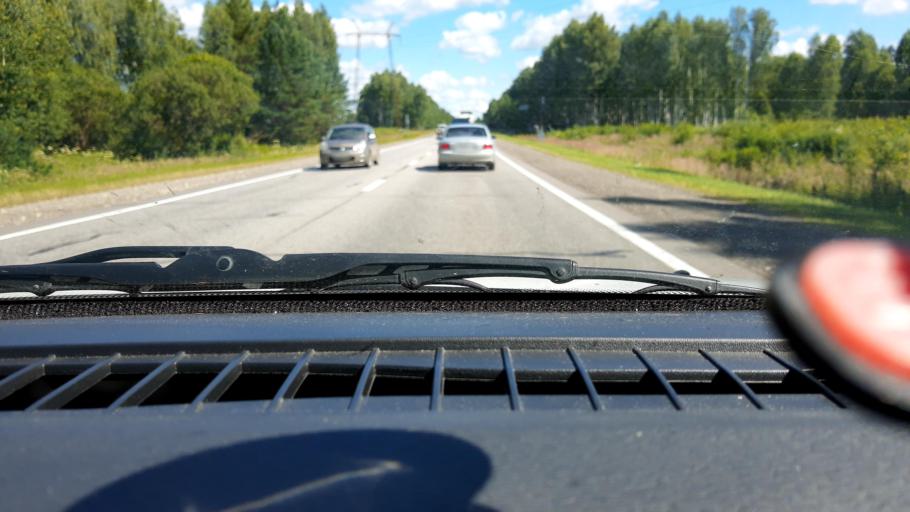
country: RU
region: Nizjnij Novgorod
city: Arzamas
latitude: 55.5559
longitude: 43.9478
